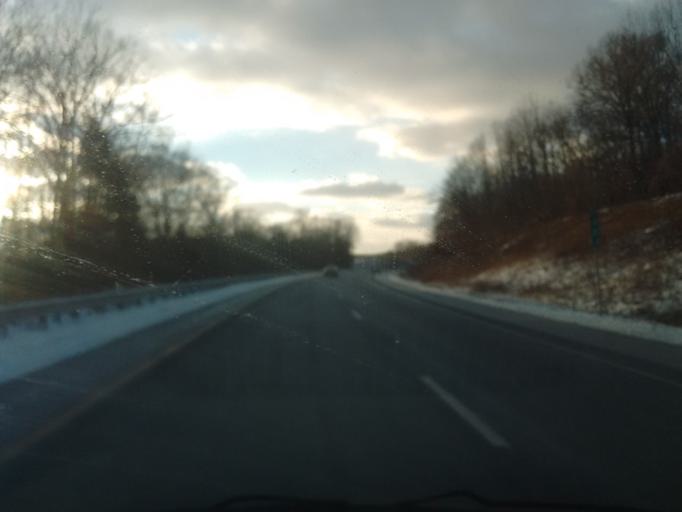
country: US
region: Pennsylvania
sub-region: Pike County
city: Milford
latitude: 41.3435
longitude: -74.7988
